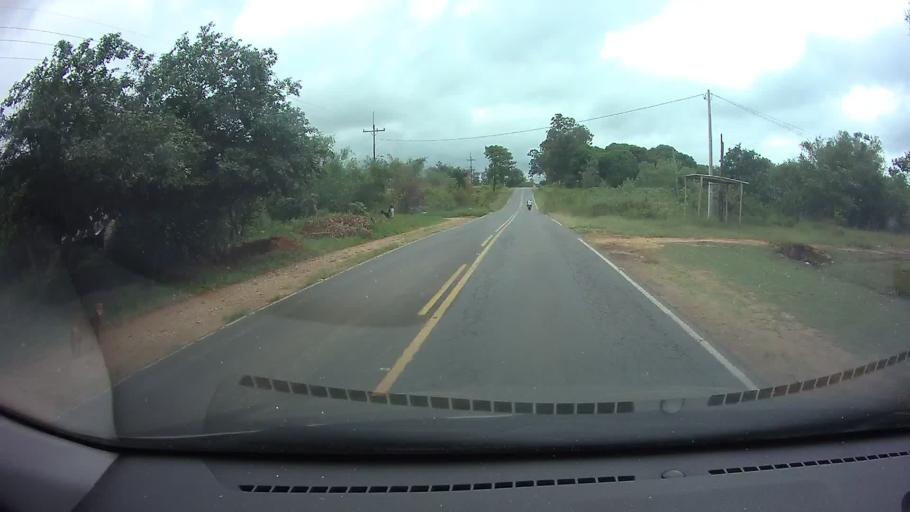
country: PY
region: Central
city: Guarambare
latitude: -25.5038
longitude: -57.4829
